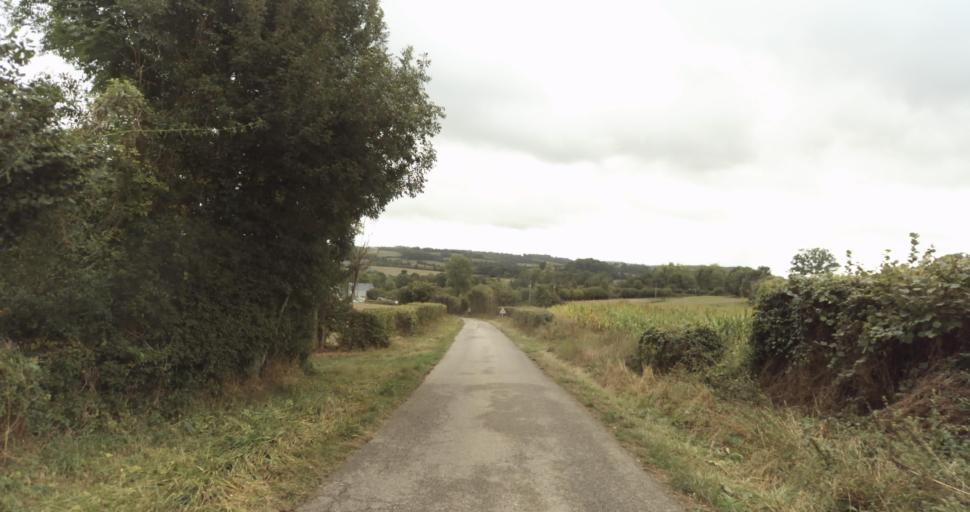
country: FR
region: Lower Normandy
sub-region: Departement de l'Orne
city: Gace
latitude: 48.8726
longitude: 0.2732
